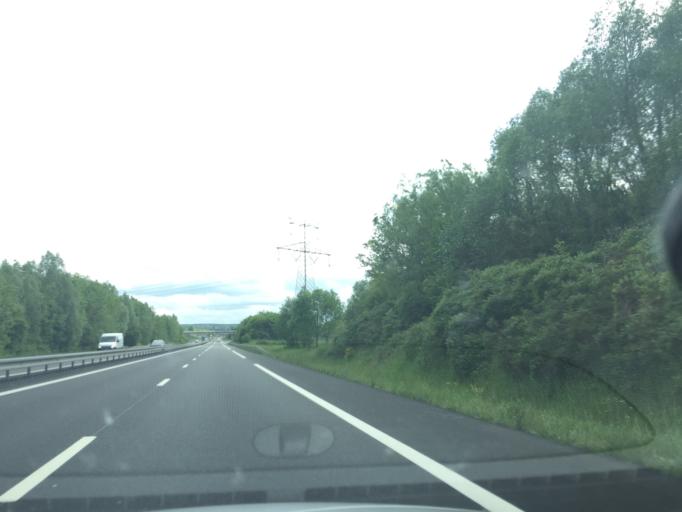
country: FR
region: Pays de la Loire
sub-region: Departement de la Sarthe
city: Ecommoy
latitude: 47.8275
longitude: 0.3063
